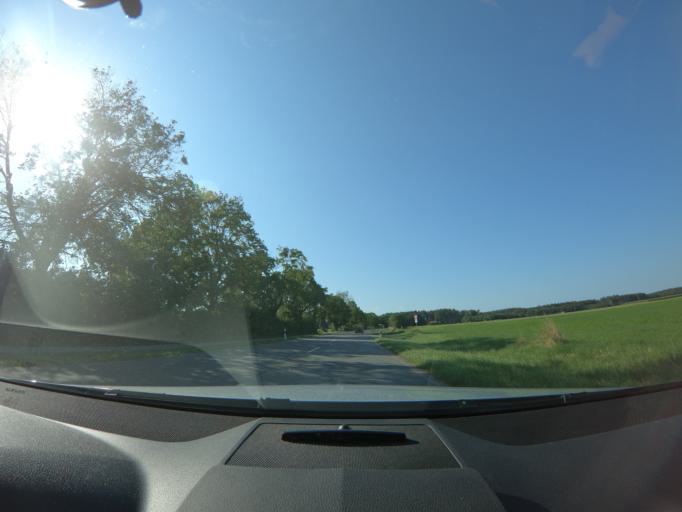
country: DE
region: Bavaria
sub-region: Upper Bavaria
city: Otterfing
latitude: 47.9161
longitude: 11.6701
